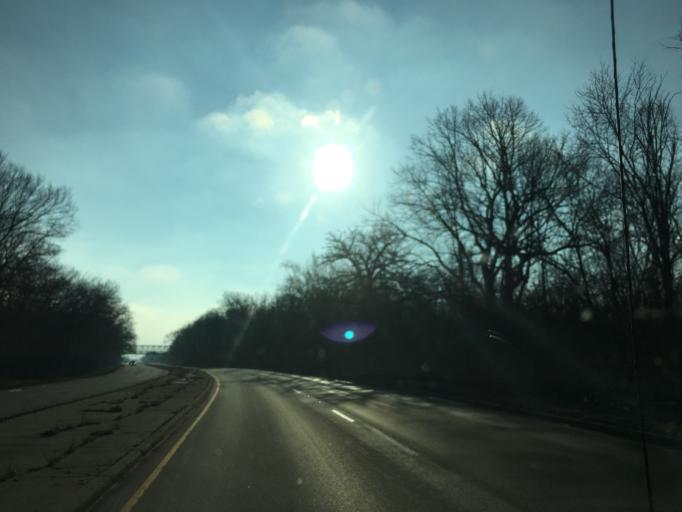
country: US
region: Illinois
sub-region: Cook County
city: Elk Grove Village
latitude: 42.0291
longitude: -87.9947
